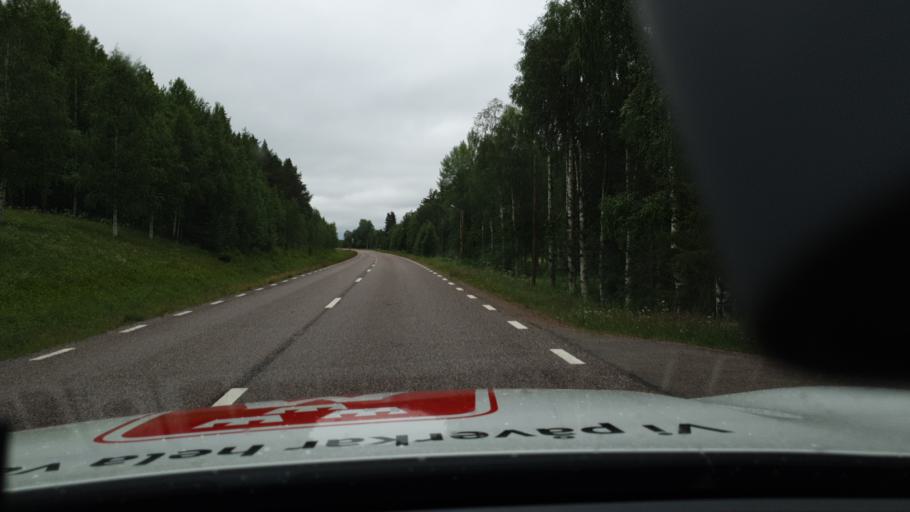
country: FI
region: Lapland
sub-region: Torniolaakso
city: Pello
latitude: 66.9466
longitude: 23.8499
